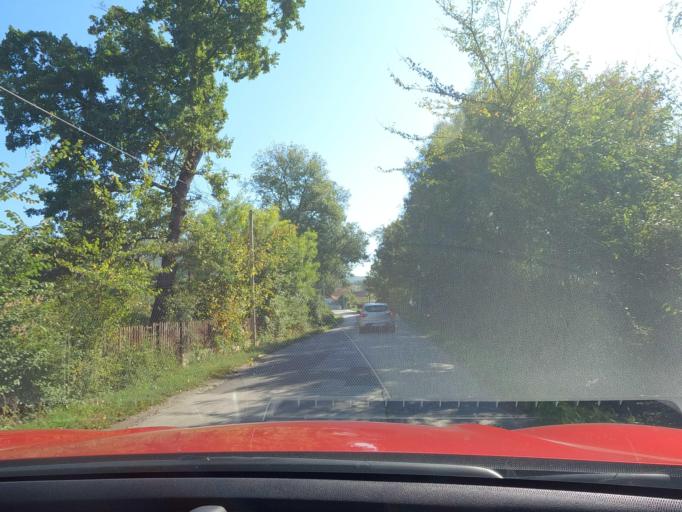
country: RS
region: Central Serbia
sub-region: Raski Okrug
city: Kraljevo
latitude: 43.7491
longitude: 20.7128
